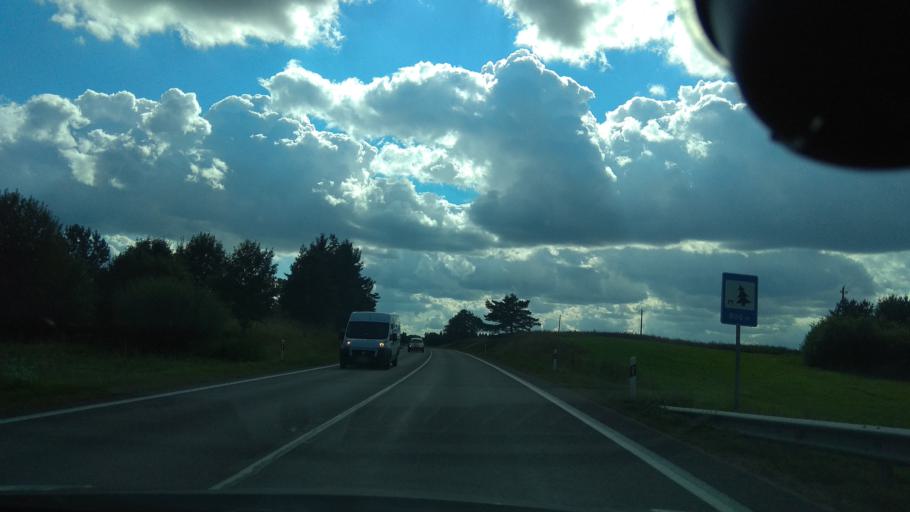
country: LT
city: Seda
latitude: 55.9955
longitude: 22.0602
